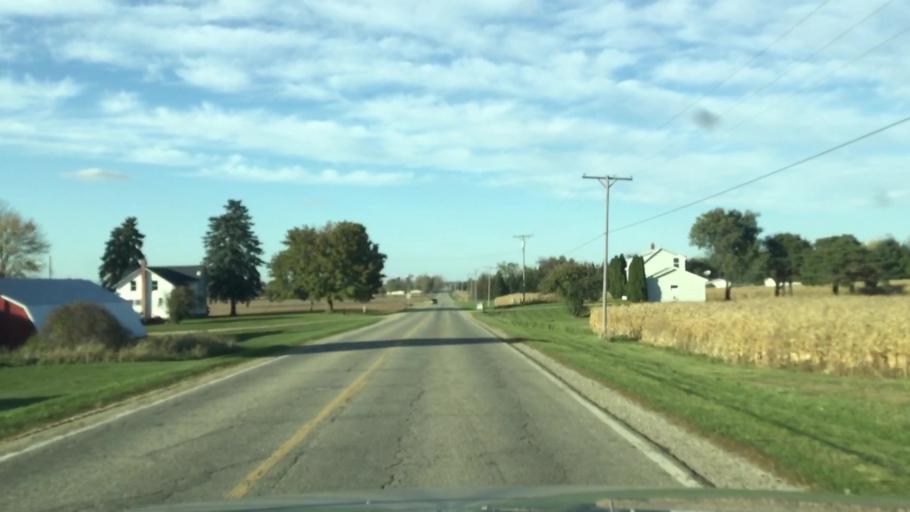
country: US
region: Michigan
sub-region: Lapeer County
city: North Branch
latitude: 43.2786
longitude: -83.1983
